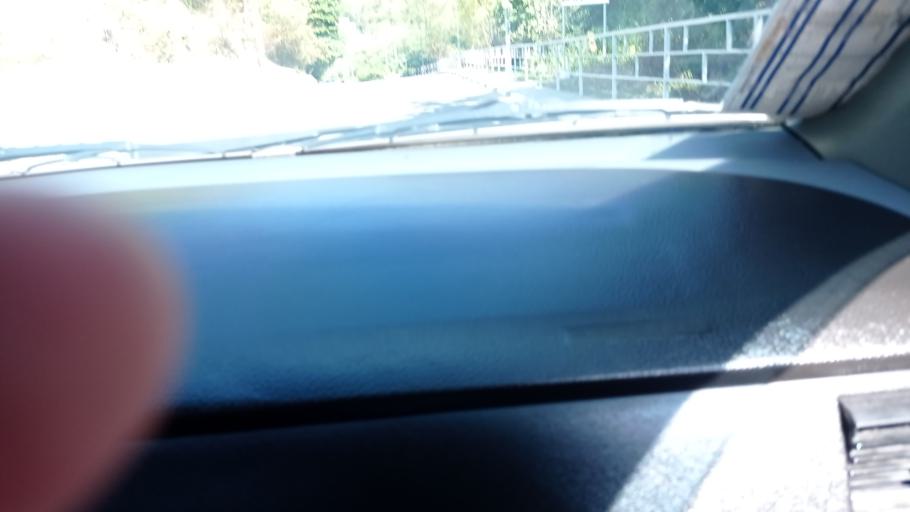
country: RU
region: Krasnodarskiy
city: Vysokoye
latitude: 43.5882
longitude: 40.0076
